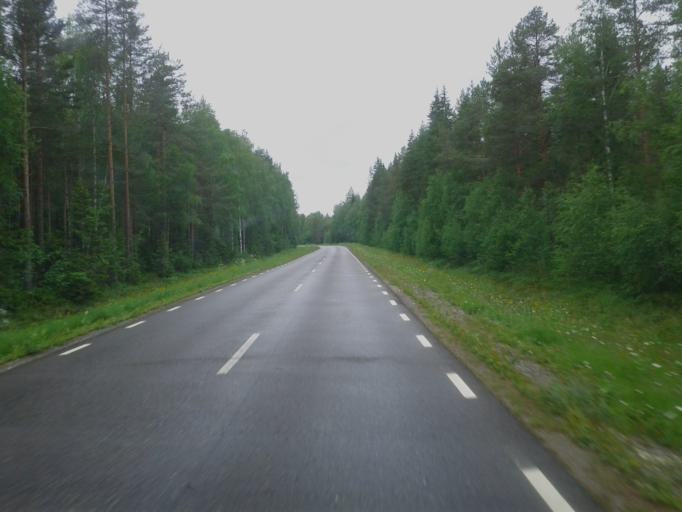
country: SE
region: Vaesterbotten
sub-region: Skelleftea Kommun
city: Kage
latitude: 64.9196
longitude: 20.8796
